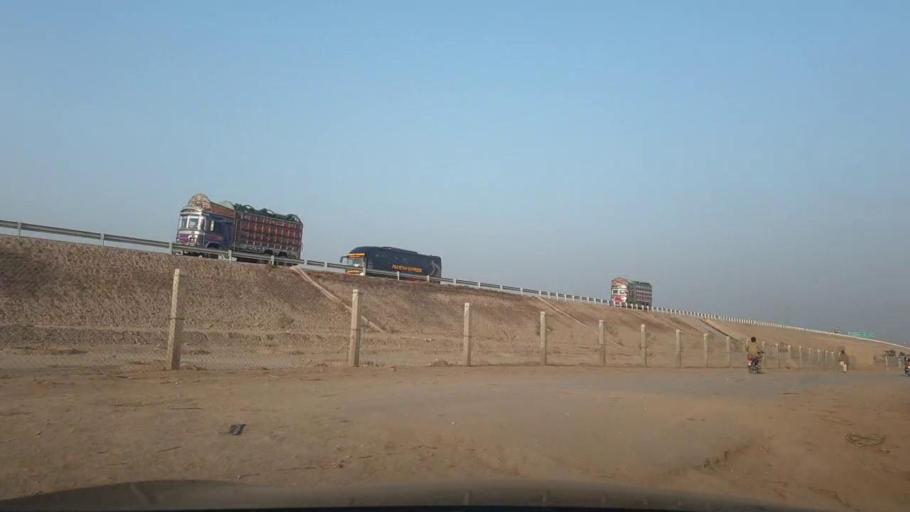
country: PK
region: Sindh
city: Ubauro
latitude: 28.3228
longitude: 69.7755
